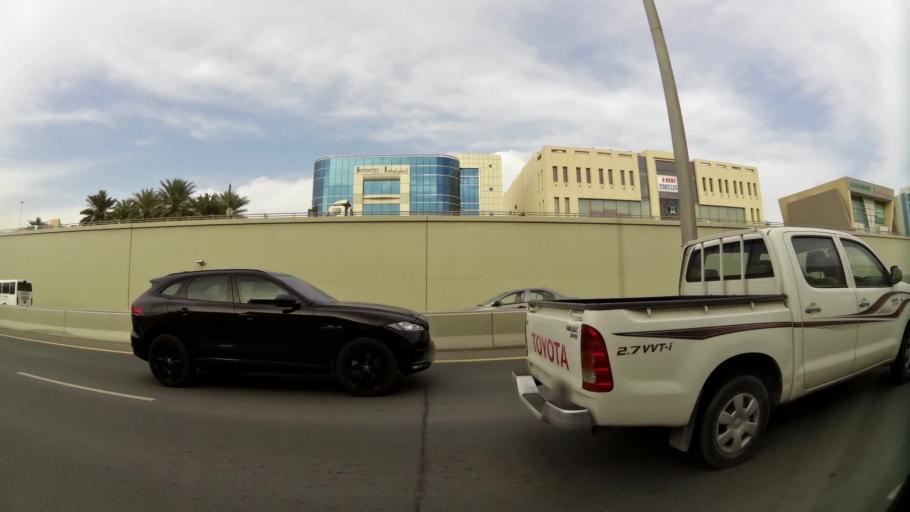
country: QA
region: Baladiyat ad Dawhah
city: Doha
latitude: 25.2740
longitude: 51.4901
